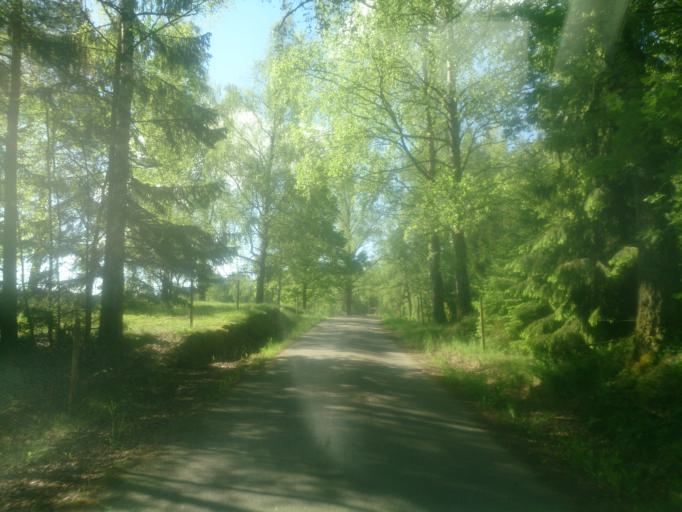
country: SE
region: OEstergoetland
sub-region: Atvidabergs Kommun
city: Atvidaberg
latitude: 58.3010
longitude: 16.0772
